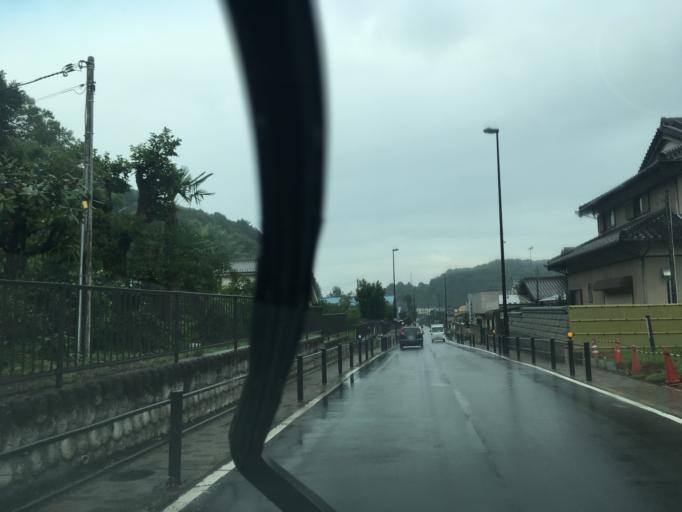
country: JP
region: Tokyo
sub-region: Machida-shi
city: Machida
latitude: 35.6005
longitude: 139.4366
